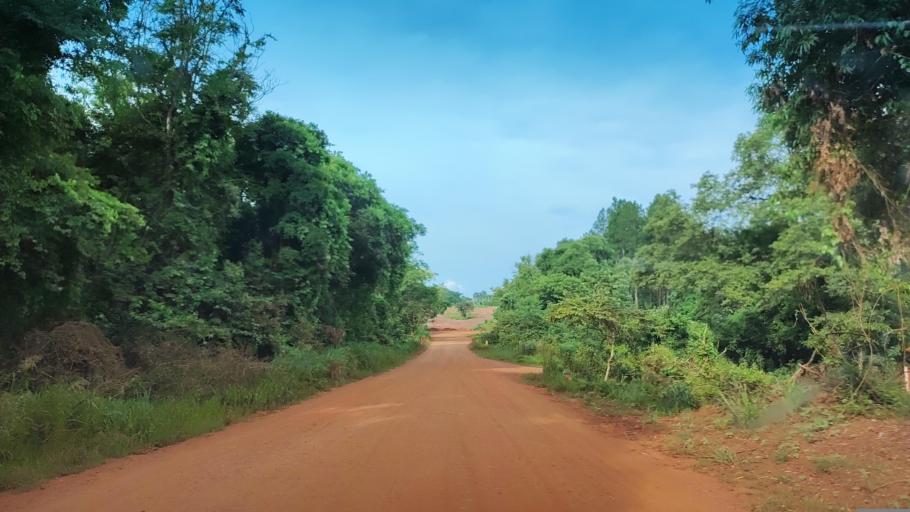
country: AR
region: Misiones
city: Gobernador Roca
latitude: -27.1379
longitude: -55.5201
